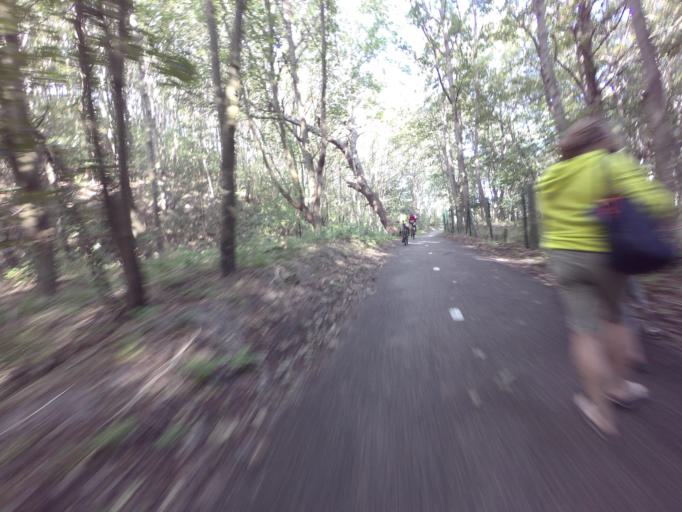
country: NL
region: Zeeland
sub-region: Gemeente Vlissingen
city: Vlissingen
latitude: 51.4925
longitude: 3.5019
